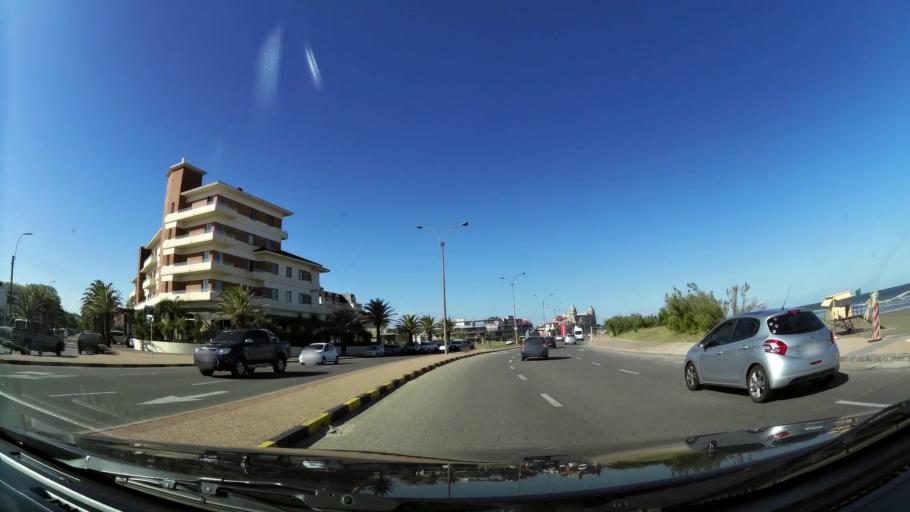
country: UY
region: Canelones
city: Barra de Carrasco
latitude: -34.8948
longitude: -56.0600
